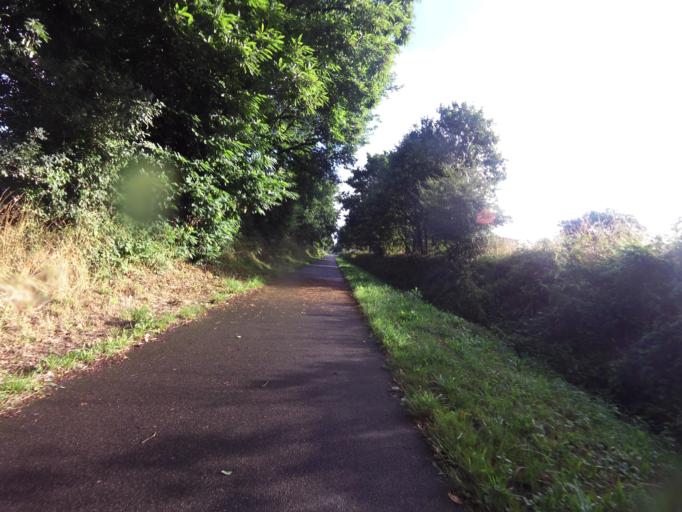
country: FR
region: Brittany
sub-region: Departement du Morbihan
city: Guillac
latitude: 47.8566
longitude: -2.4397
